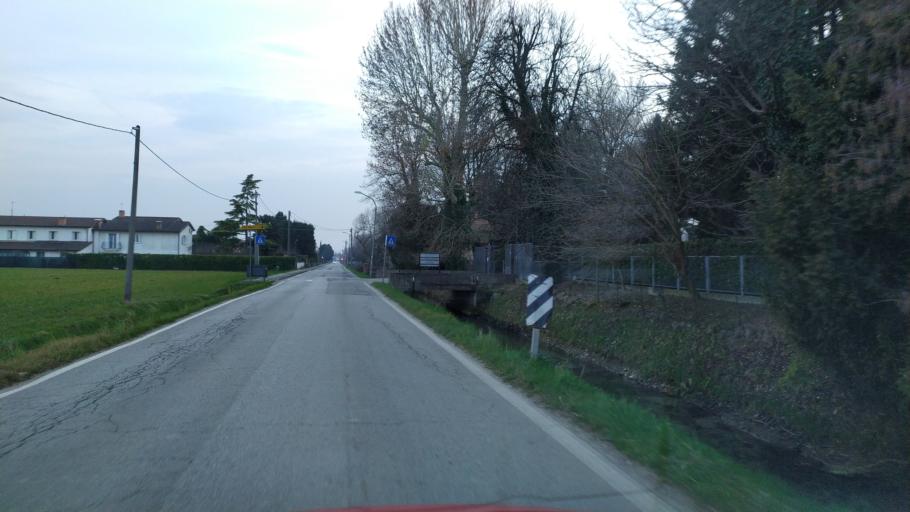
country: IT
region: Veneto
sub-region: Provincia di Vicenza
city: Vigardolo
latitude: 45.6112
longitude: 11.5868
